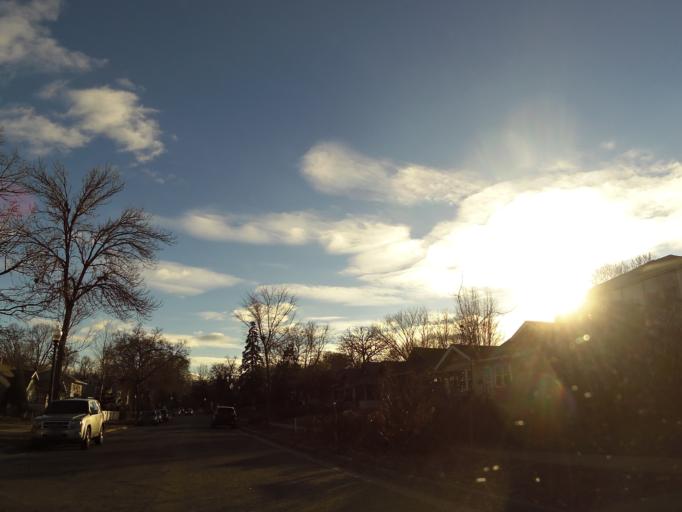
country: US
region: Minnesota
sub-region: Hennepin County
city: Richfield
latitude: 44.9134
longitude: -93.2730
